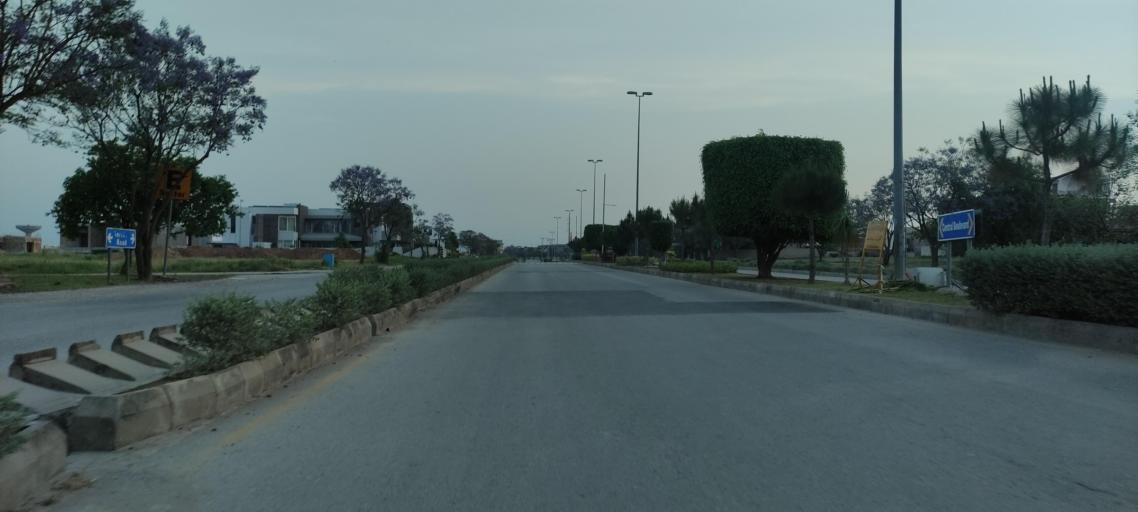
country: PK
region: Punjab
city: Rawalpindi
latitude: 33.5242
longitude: 73.1653
